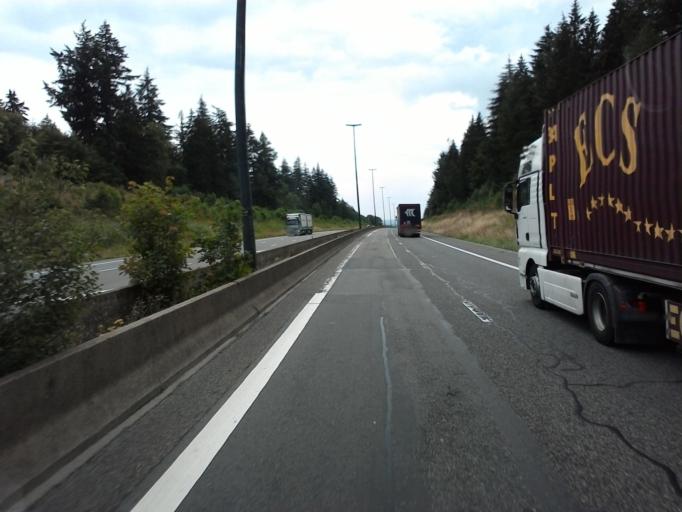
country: BE
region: Wallonia
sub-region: Province du Luxembourg
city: Houffalize
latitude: 50.2011
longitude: 5.7793
